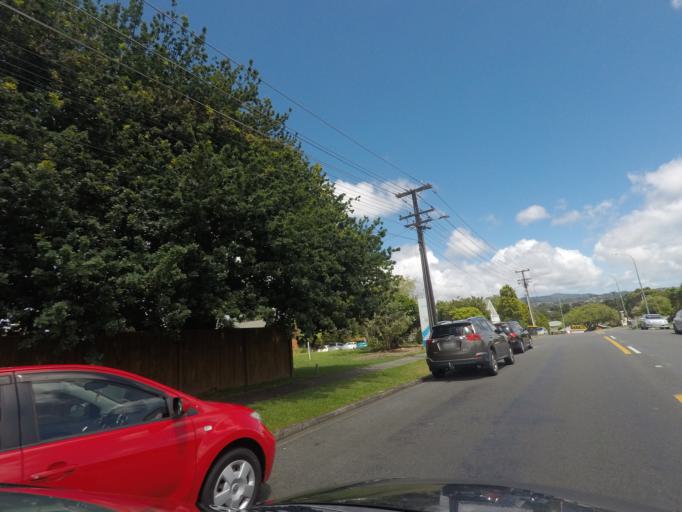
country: NZ
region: Auckland
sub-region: Auckland
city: Rosebank
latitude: -36.8763
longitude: 174.6448
